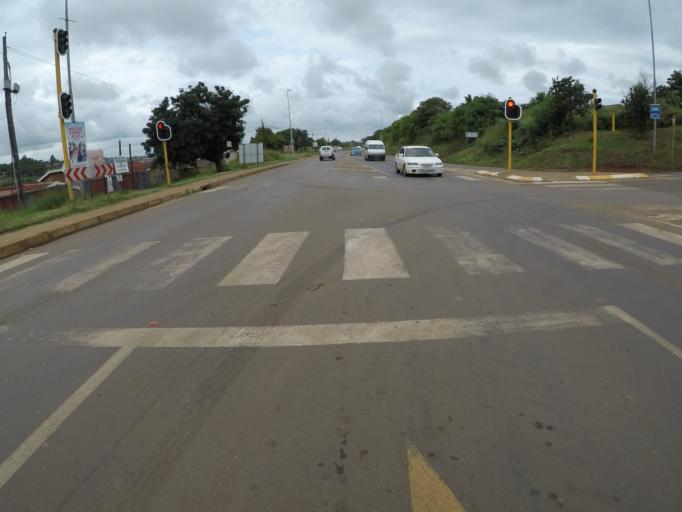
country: ZA
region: KwaZulu-Natal
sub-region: uThungulu District Municipality
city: Empangeni
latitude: -28.7738
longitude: 31.8655
